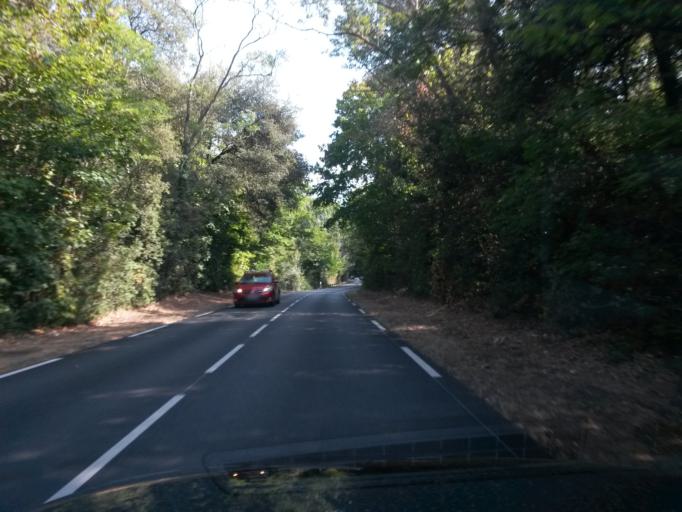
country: FR
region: Pays de la Loire
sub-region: Departement de la Vendee
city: Olonne-sur-Mer
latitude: 46.5698
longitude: -1.8212
